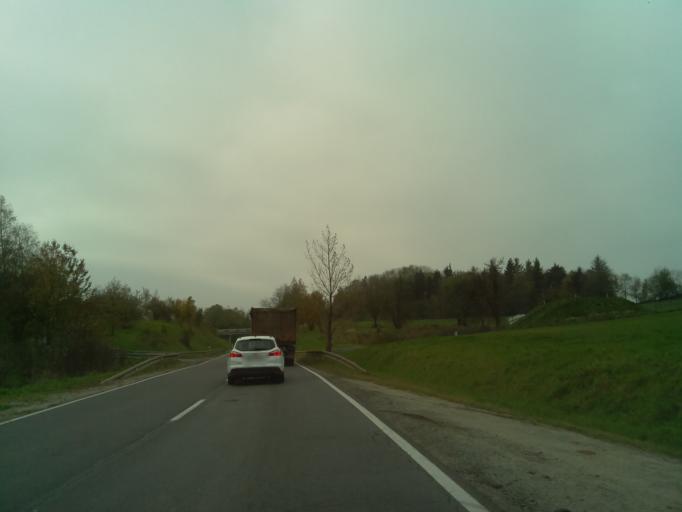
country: PL
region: Lower Silesian Voivodeship
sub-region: Powiat walbrzyski
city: Stare Bogaczowice
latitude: 50.9125
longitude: 16.2332
